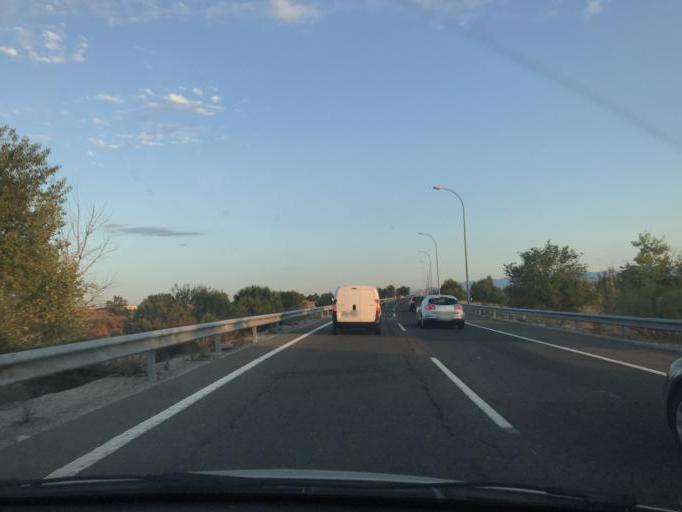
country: ES
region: Madrid
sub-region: Provincia de Madrid
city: San Sebastian de los Reyes
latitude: 40.5444
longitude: -3.5674
